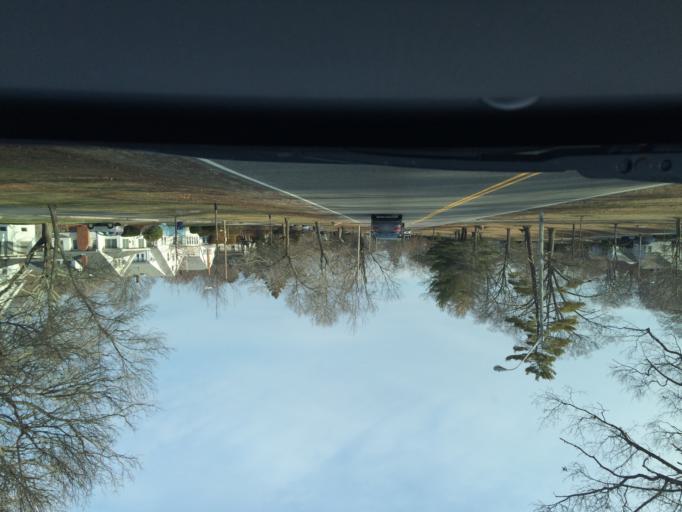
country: US
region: Massachusetts
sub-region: Suffolk County
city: Jamaica Plain
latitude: 42.2810
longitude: -71.1446
